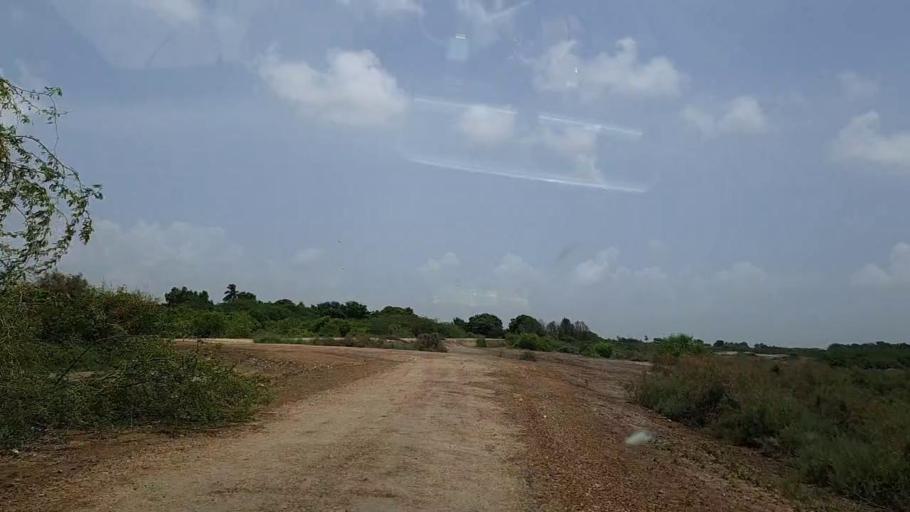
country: PK
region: Sindh
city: Keti Bandar
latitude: 24.1660
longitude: 67.5438
